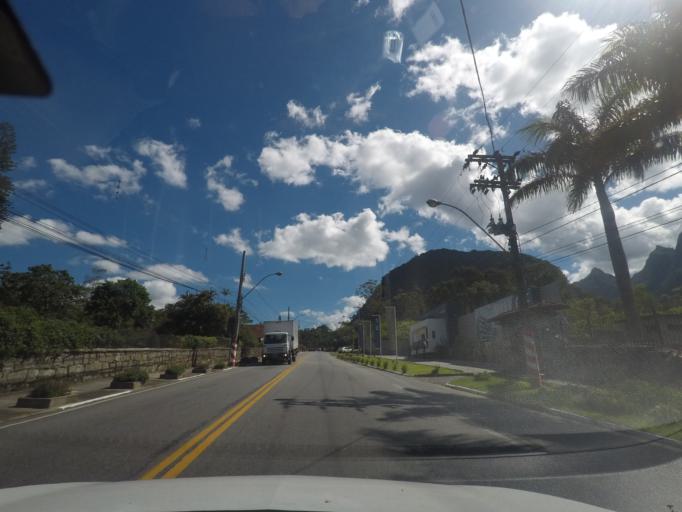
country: BR
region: Rio de Janeiro
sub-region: Teresopolis
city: Teresopolis
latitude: -22.4457
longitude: -42.9817
